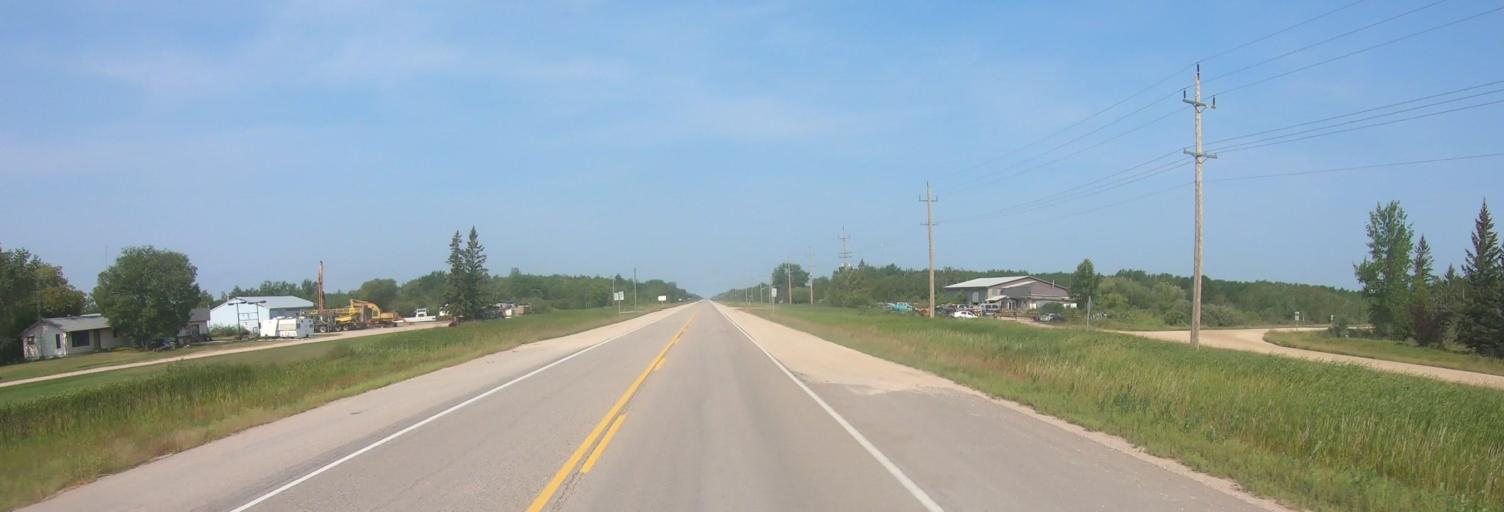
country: CA
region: Manitoba
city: La Broquerie
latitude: 49.2838
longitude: -96.5100
